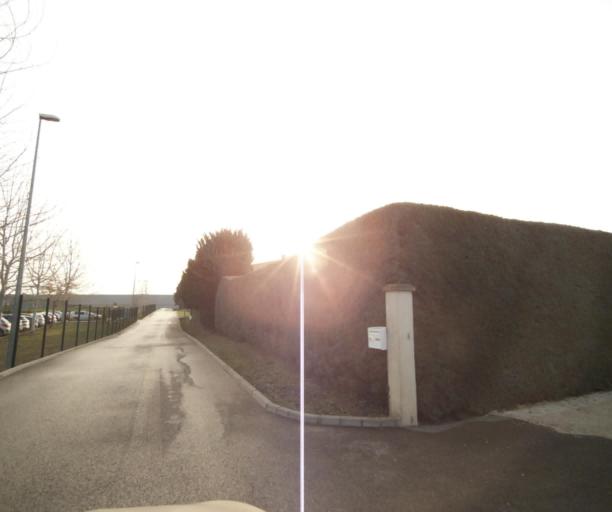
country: FR
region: Provence-Alpes-Cote d'Azur
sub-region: Departement des Bouches-du-Rhone
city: Rousset
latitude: 43.4655
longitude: 5.5987
